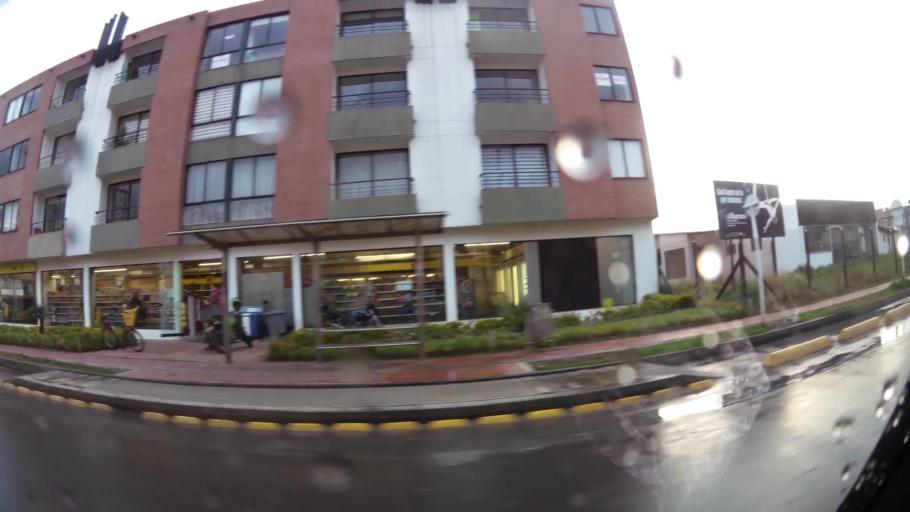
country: CO
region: Cundinamarca
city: Chia
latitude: 4.8666
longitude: -74.0501
